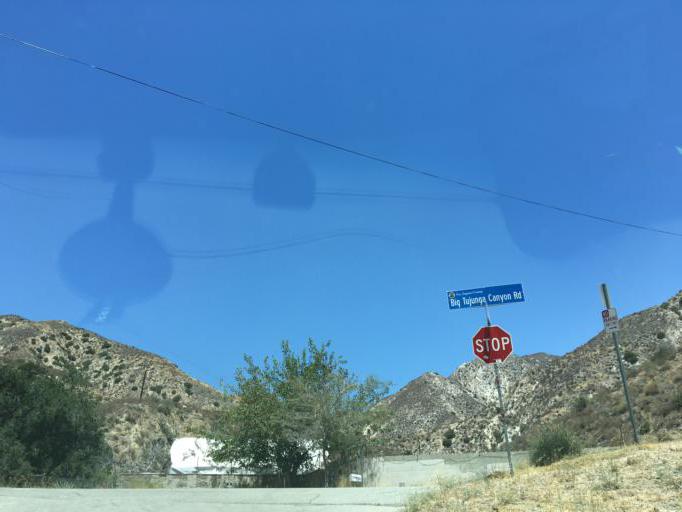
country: US
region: California
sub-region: Los Angeles County
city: La Crescenta-Montrose
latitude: 34.3025
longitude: -118.2558
